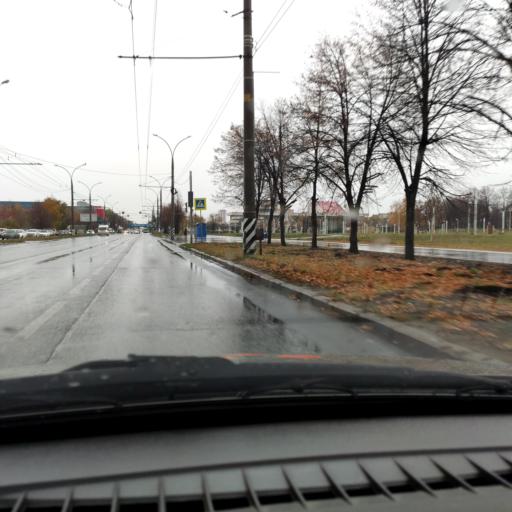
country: RU
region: Samara
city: Tol'yatti
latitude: 53.5131
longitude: 49.2724
